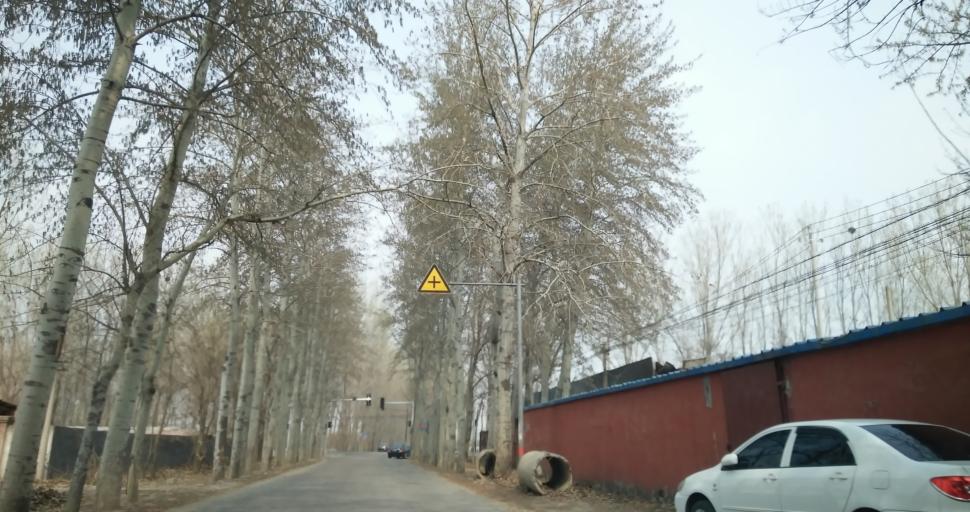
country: CN
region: Beijing
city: Qingyundian
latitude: 39.6868
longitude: 116.5056
